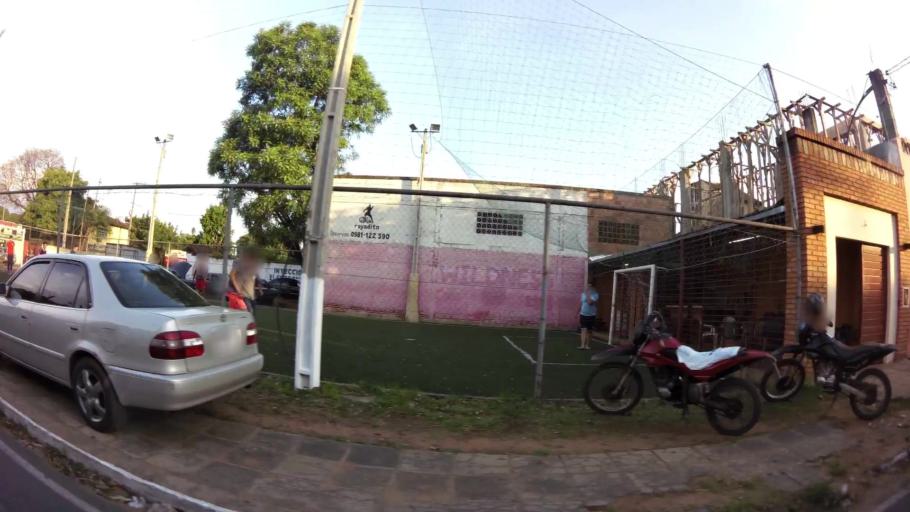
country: PY
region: Central
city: San Lorenzo
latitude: -25.3478
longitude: -57.5038
